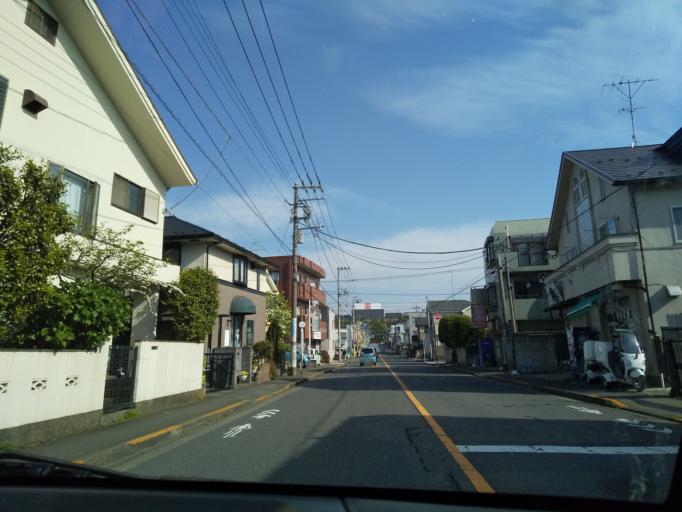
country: JP
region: Tokyo
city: Hino
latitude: 35.6700
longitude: 139.3845
